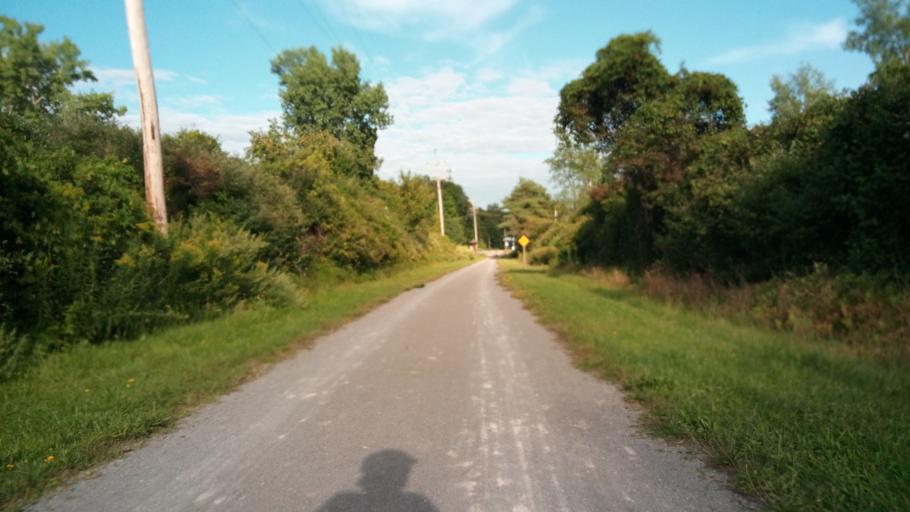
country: US
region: New York
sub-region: Ontario County
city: Victor
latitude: 43.0031
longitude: -77.4847
